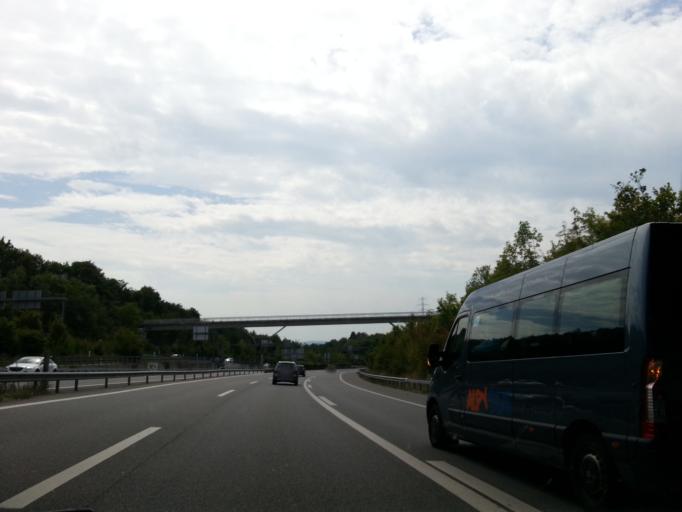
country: CH
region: Geneva
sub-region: Geneva
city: Les Avanchets
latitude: 46.2173
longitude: 6.0986
